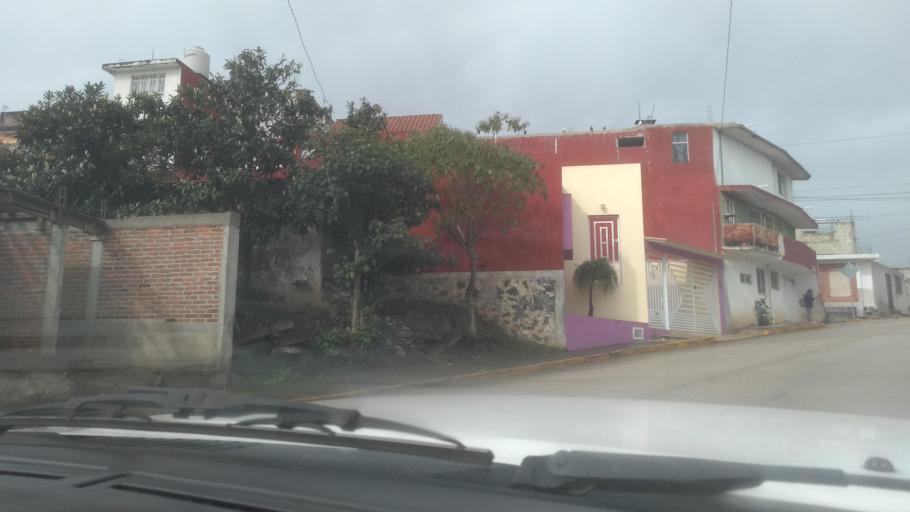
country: MX
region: Veracruz
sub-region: Xalapa
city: Colonia Santa Barbara
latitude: 19.5061
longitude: -96.8723
